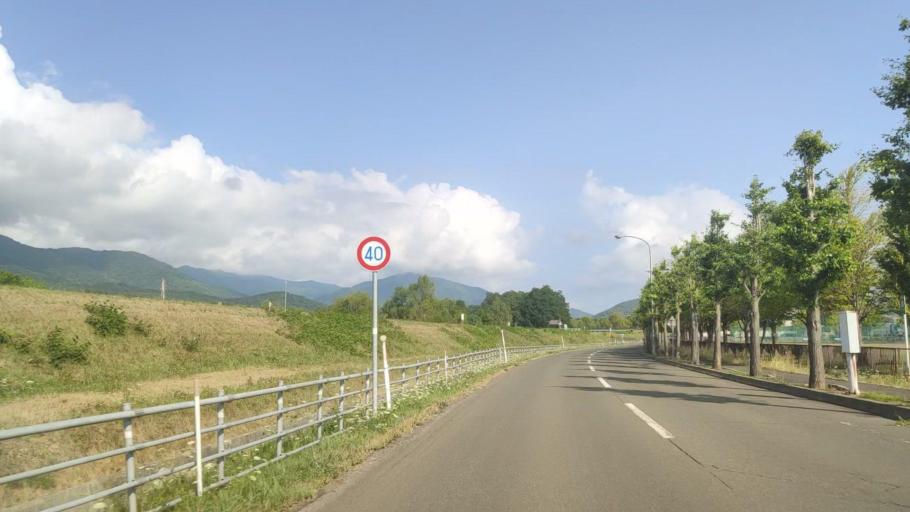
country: JP
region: Hokkaido
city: Shimo-furano
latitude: 43.3428
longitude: 142.3773
